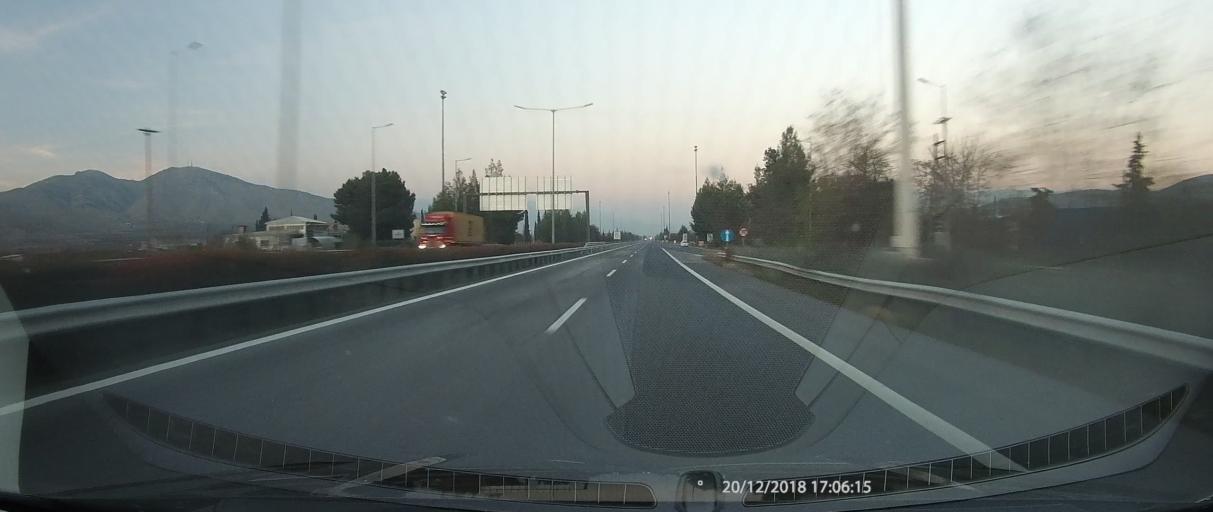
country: GR
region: Thessaly
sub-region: Nomos Larisis
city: Makrychori
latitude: 39.7556
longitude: 22.4763
